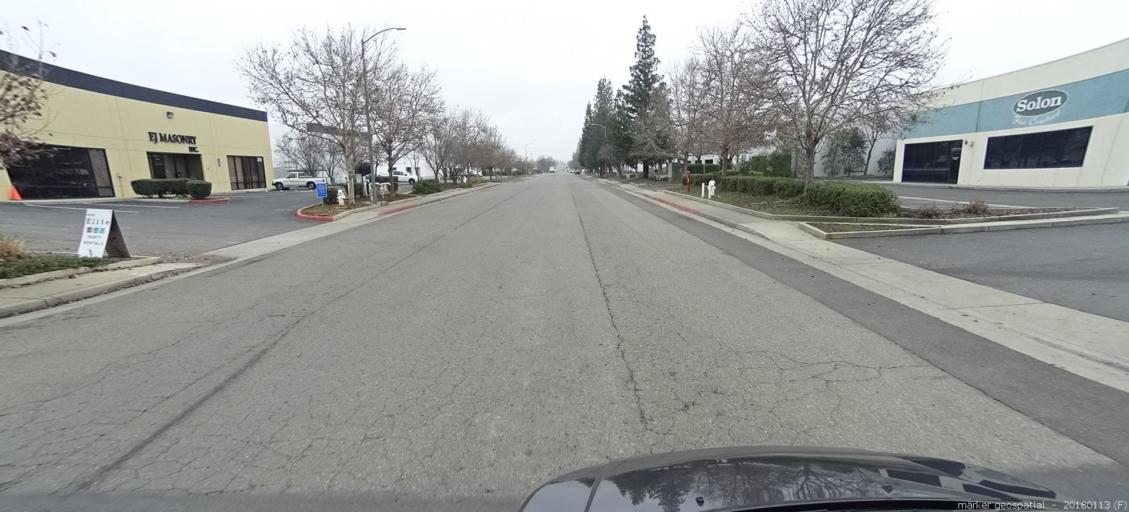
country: US
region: California
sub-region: Sacramento County
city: Gold River
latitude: 38.5877
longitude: -121.2563
